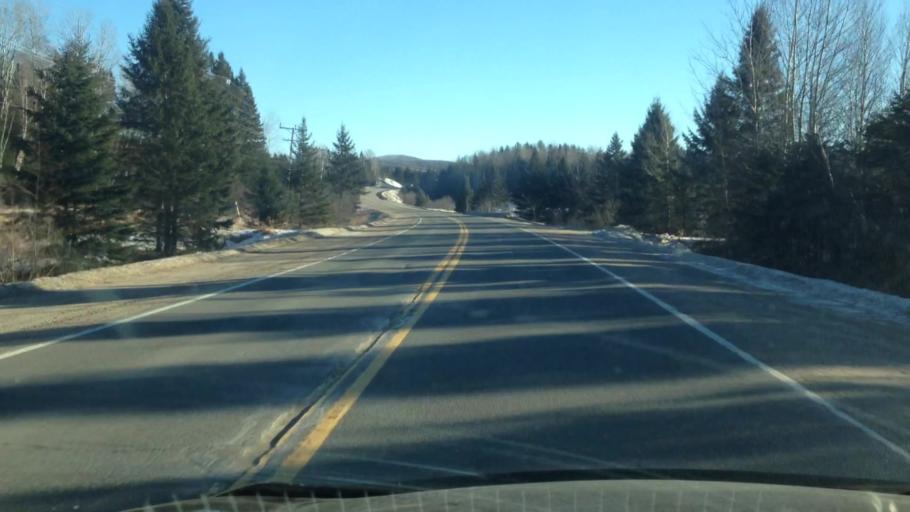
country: CA
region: Quebec
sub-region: Laurentides
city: Mont-Tremblant
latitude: 46.0539
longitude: -74.6153
